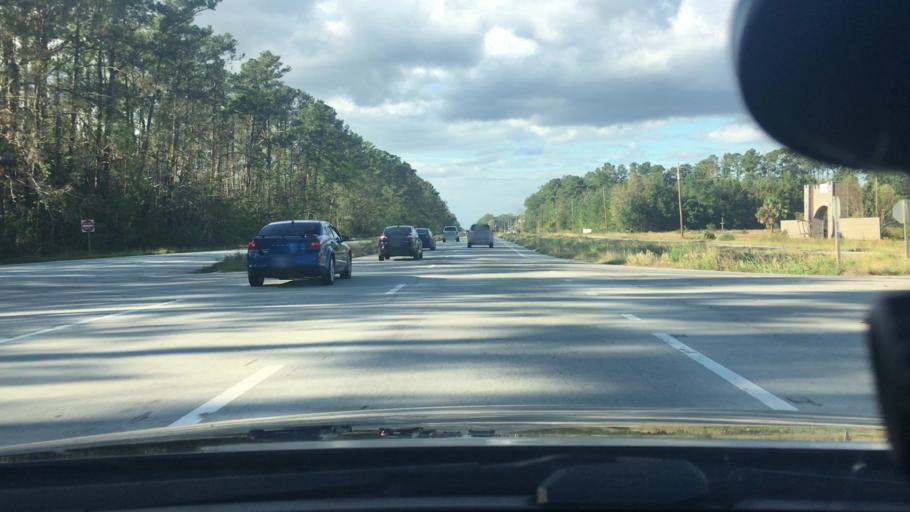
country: US
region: North Carolina
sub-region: Craven County
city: Fairfield Harbour
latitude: 35.0308
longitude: -77.0032
